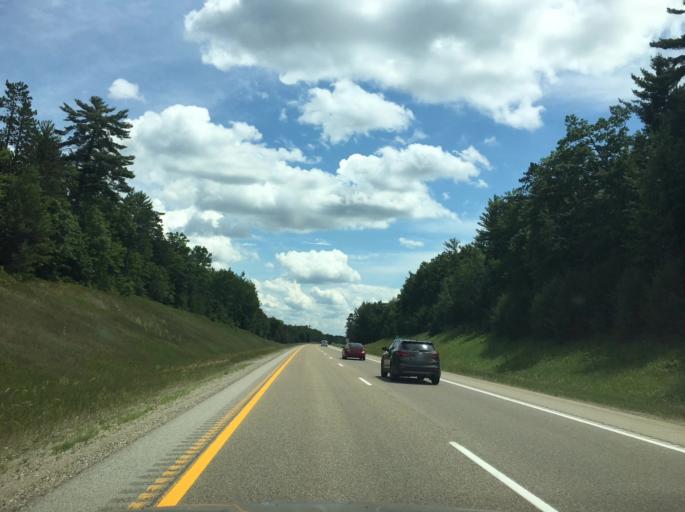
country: US
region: Michigan
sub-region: Roscommon County
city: Roscommon
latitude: 44.5371
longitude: -84.6877
